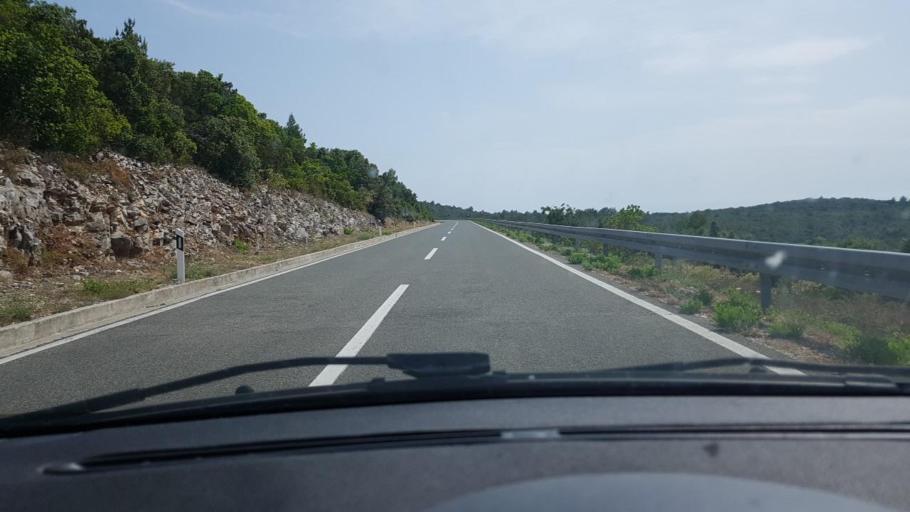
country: HR
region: Dubrovacko-Neretvanska
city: Smokvica
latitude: 42.9533
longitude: 16.9425
